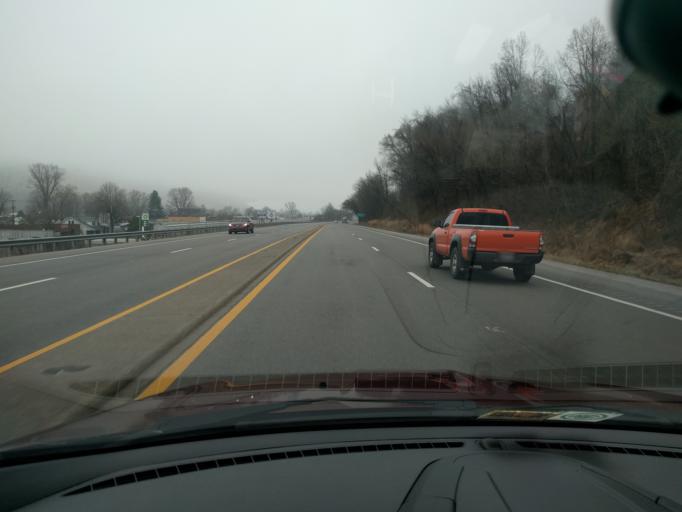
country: US
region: West Virginia
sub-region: Kanawha County
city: Rand
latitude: 38.2765
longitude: -81.5639
